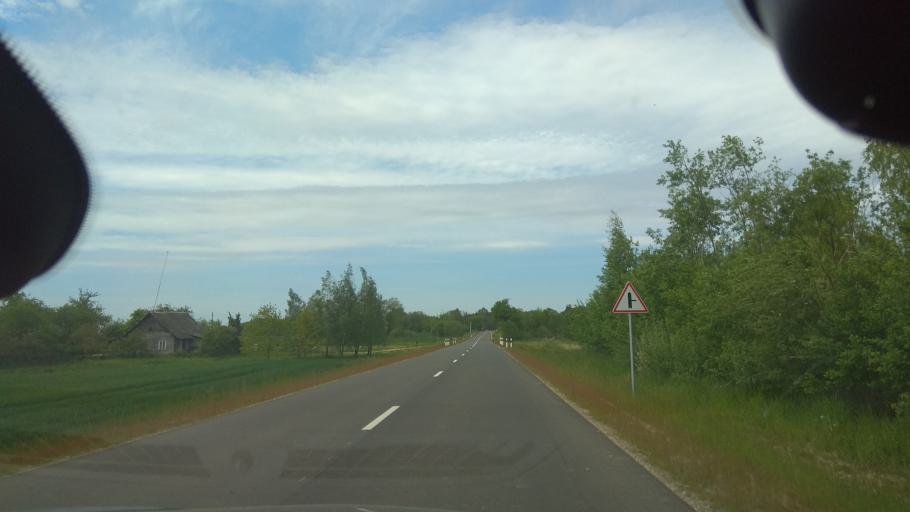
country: LT
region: Vilnius County
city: Ukmerge
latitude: 55.1163
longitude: 24.6352
